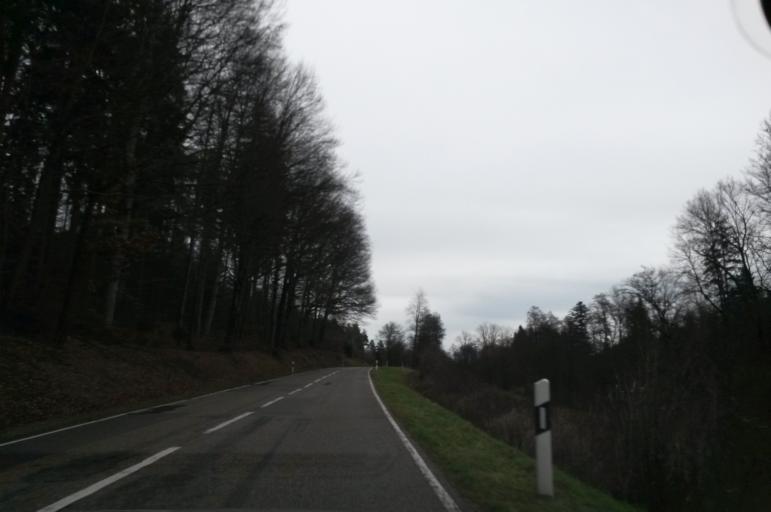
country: DE
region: Baden-Wuerttemberg
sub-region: Karlsruhe Region
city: Dobel
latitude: 48.8413
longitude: 8.4804
